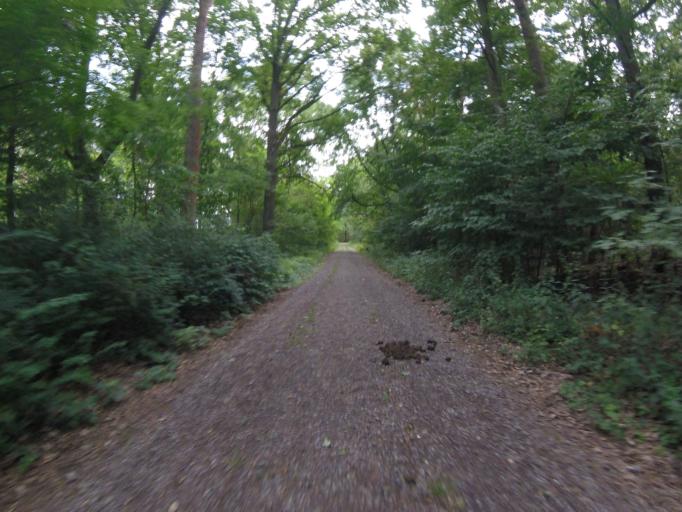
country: DE
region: Brandenburg
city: Gross Koris
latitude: 52.1520
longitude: 13.6741
